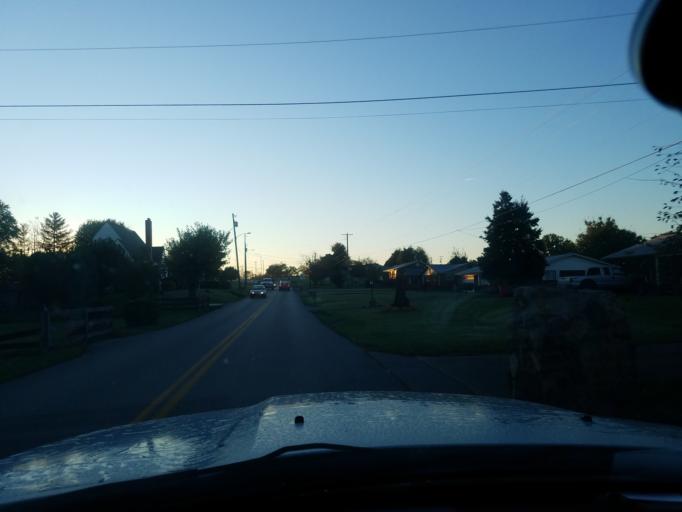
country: US
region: Kentucky
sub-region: Laurel County
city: London
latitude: 37.1013
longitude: -84.0896
